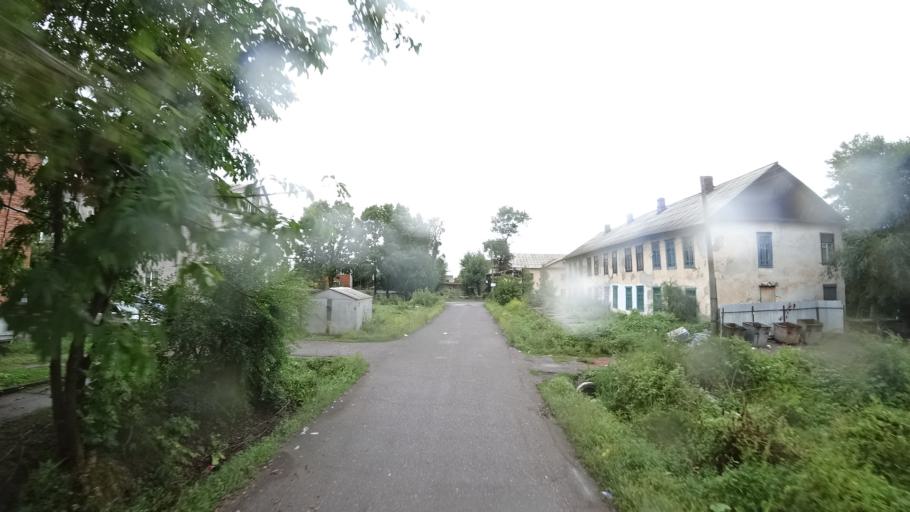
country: RU
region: Primorskiy
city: Monastyrishche
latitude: 44.1946
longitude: 132.4248
